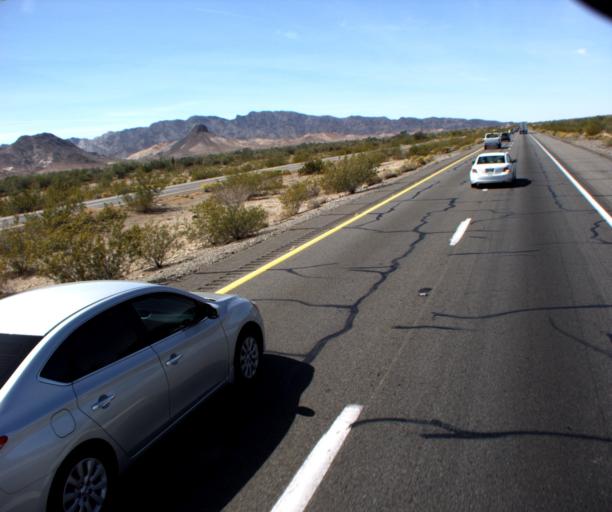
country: US
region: Arizona
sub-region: La Paz County
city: Quartzsite
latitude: 33.6533
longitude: -114.2870
